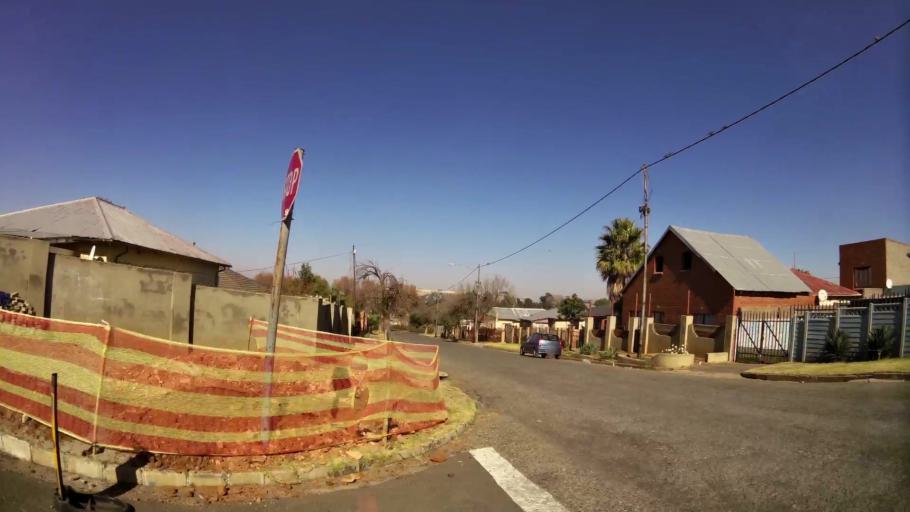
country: ZA
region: Gauteng
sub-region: City of Johannesburg Metropolitan Municipality
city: Johannesburg
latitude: -26.1988
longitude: 27.9903
